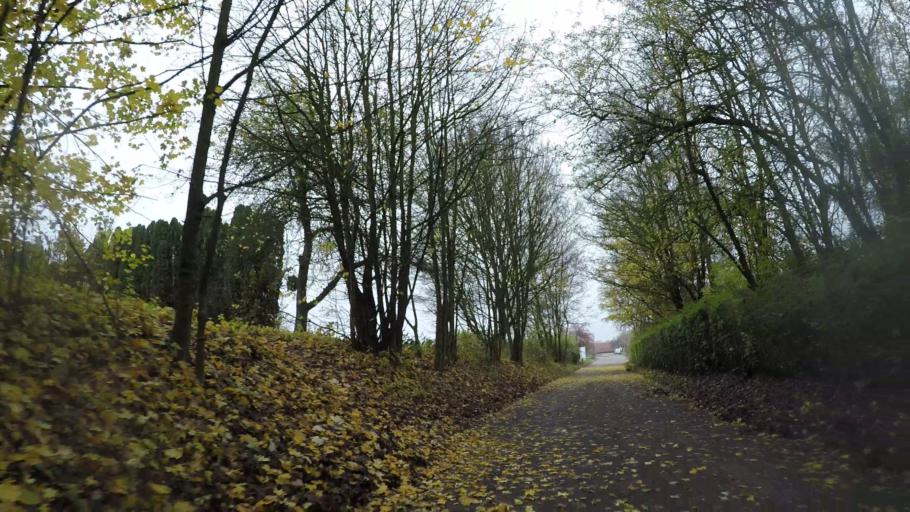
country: DE
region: Baden-Wuerttemberg
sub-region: Tuebingen Region
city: Sickenhausen
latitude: 48.5221
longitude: 9.1962
